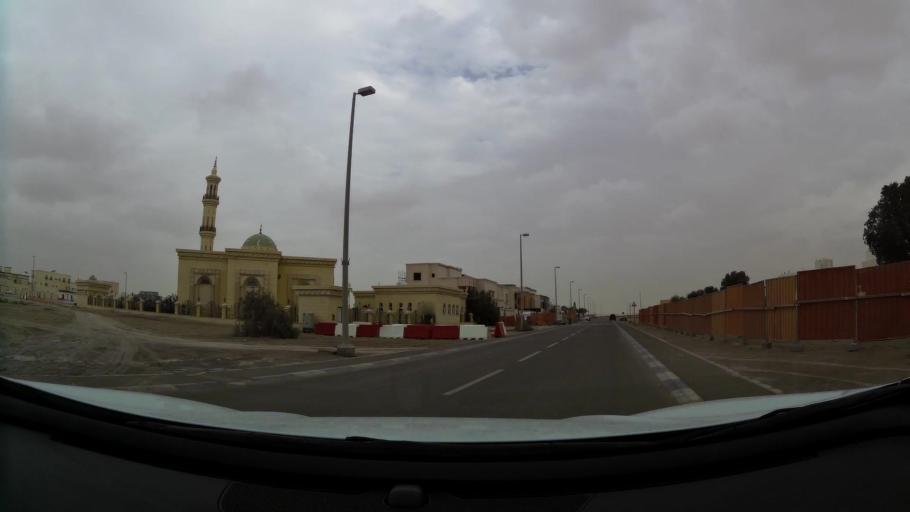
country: AE
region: Abu Dhabi
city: Abu Dhabi
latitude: 24.3574
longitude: 54.6602
